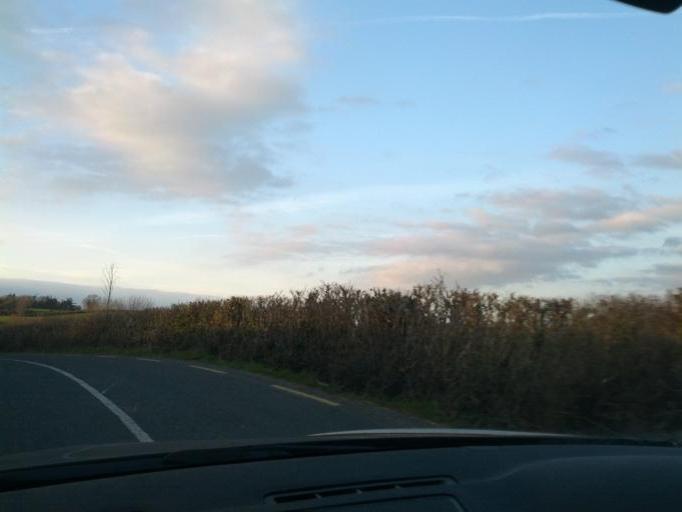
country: IE
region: Munster
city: Nenagh Bridge
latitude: 52.9512
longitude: -8.2296
